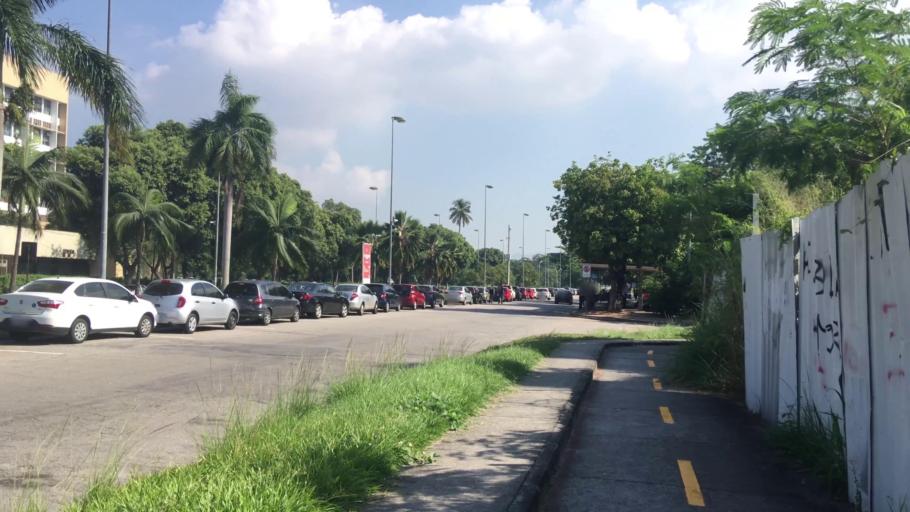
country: BR
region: Rio de Janeiro
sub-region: Rio De Janeiro
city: Rio de Janeiro
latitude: -22.8552
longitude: -43.2315
